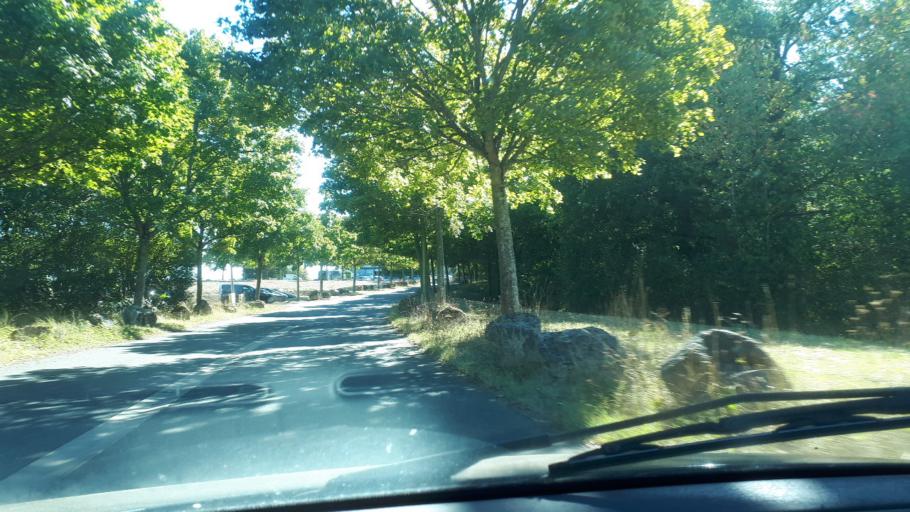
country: FR
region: Centre
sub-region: Departement du Loir-et-Cher
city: Naveil
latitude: 47.8137
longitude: 1.0254
